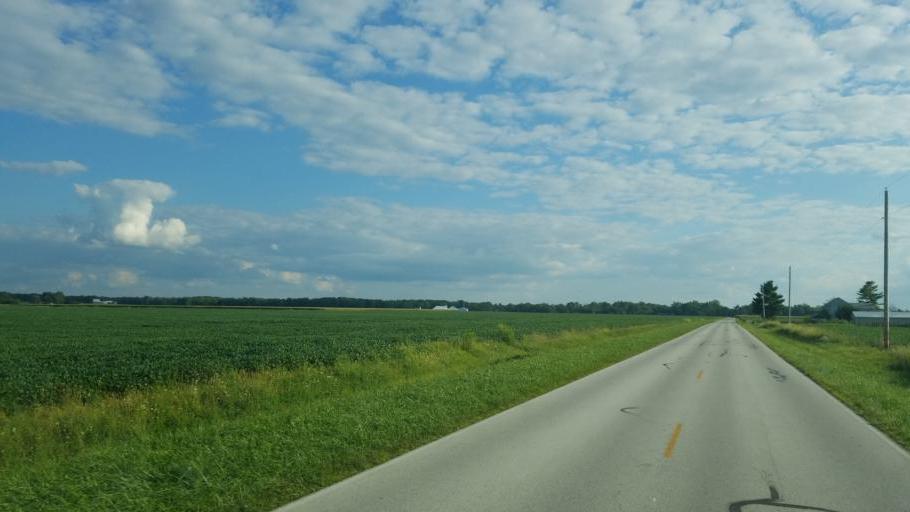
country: US
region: Ohio
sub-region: Seneca County
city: Tiffin
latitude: 41.1771
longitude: -83.1217
